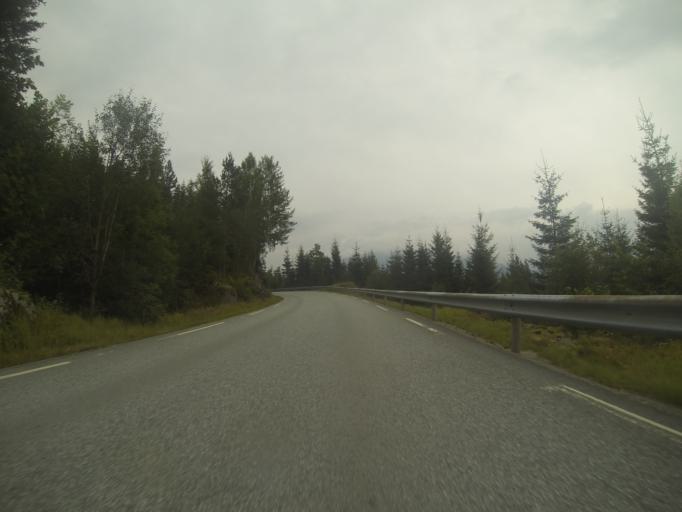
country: NO
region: Rogaland
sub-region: Suldal
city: Sand
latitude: 59.5089
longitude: 6.2116
